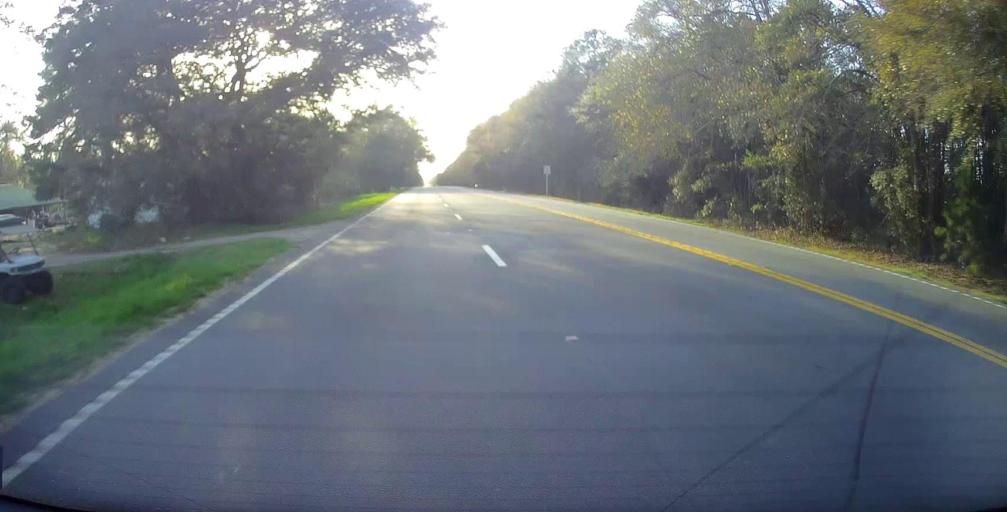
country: US
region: Georgia
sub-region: Evans County
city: Claxton
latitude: 32.1525
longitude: -81.8093
